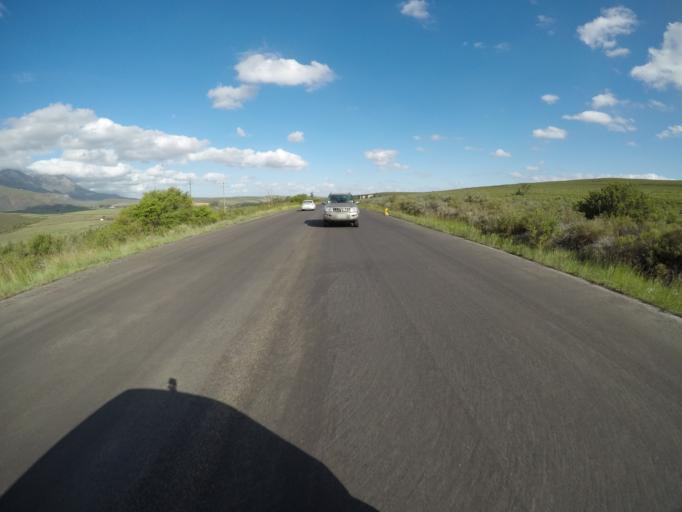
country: ZA
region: Western Cape
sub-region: Cape Winelands District Municipality
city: Ashton
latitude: -33.9341
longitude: 20.2109
